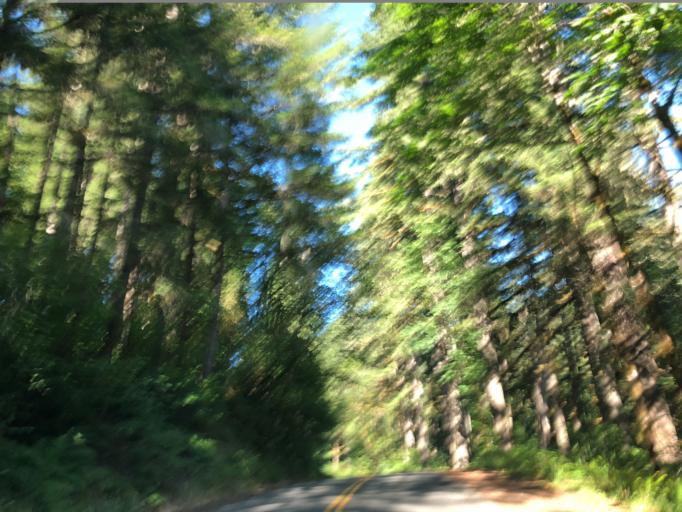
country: US
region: Oregon
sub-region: Linn County
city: Sweet Home
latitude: 44.4648
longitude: -122.6802
